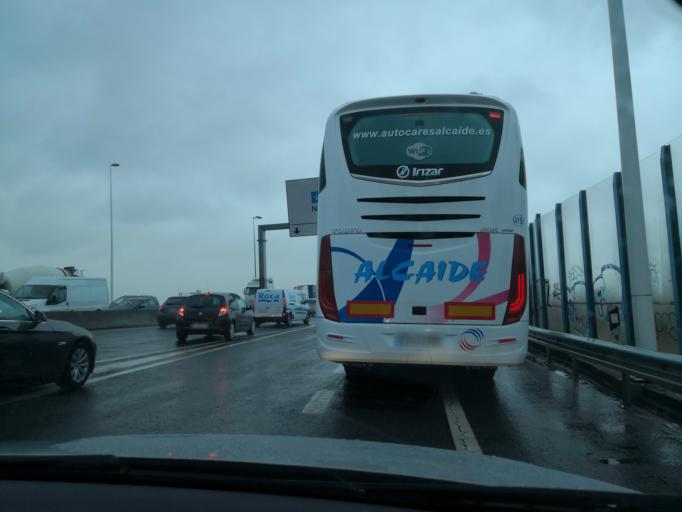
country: PT
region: Lisbon
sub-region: Loures
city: Sacavem
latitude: 38.7878
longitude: -9.1044
